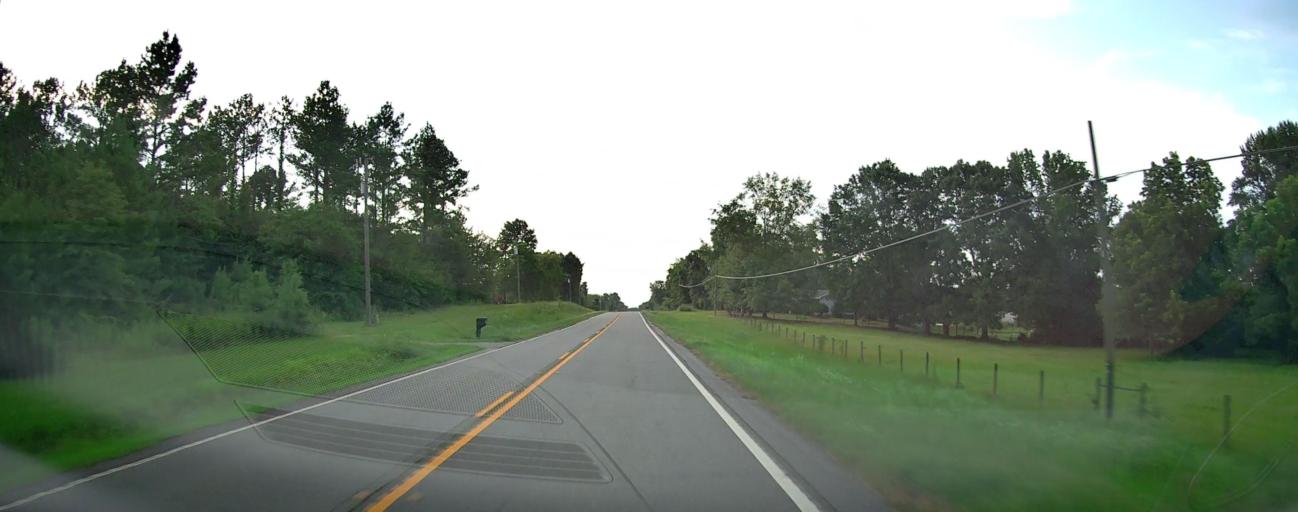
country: US
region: Georgia
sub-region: Taylor County
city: Reynolds
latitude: 32.6026
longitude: -84.0948
